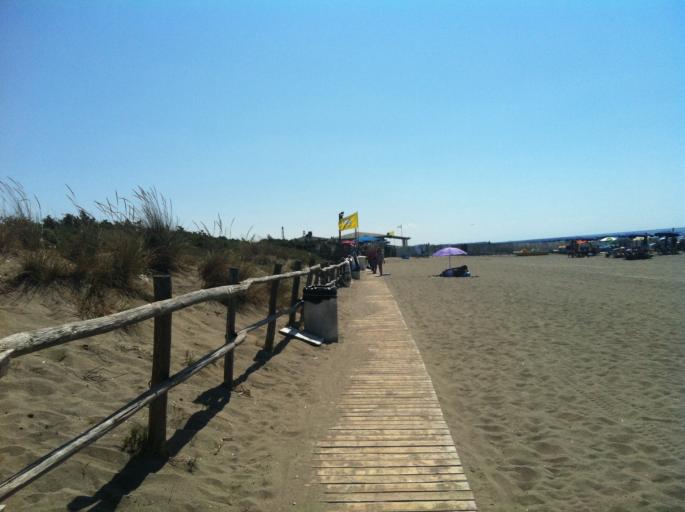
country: IT
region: Latium
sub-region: Provincia di Viterbo
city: Pescia Romana
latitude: 42.3797
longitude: 11.4437
